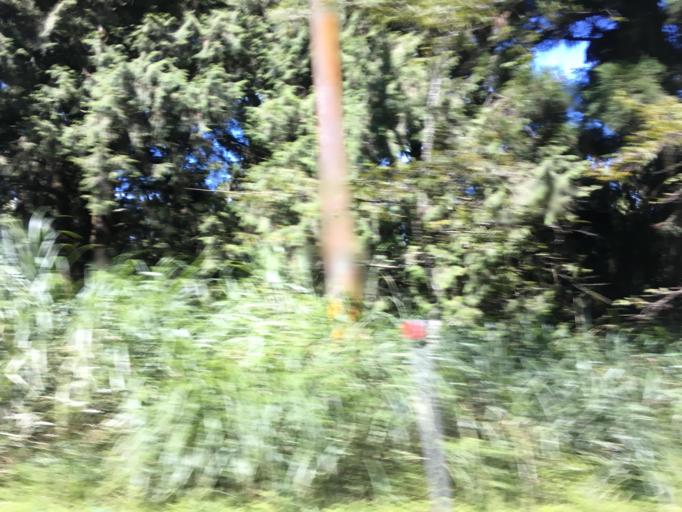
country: TW
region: Taiwan
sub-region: Yilan
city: Yilan
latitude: 24.5215
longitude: 121.5187
